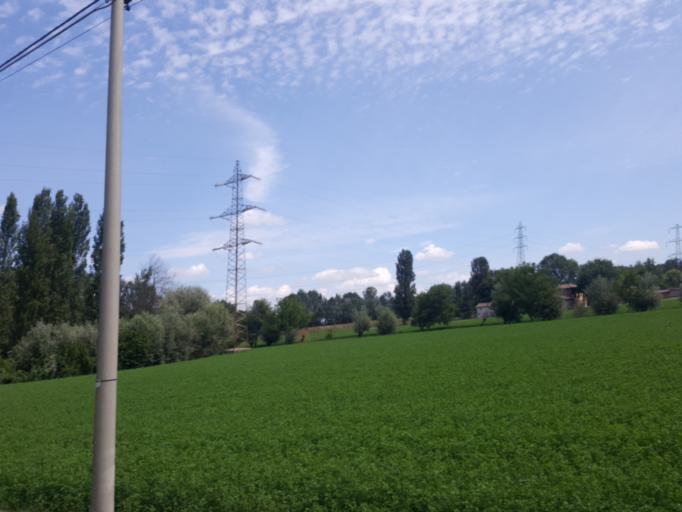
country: IT
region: Emilia-Romagna
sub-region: Provincia di Bologna
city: Anzola dell'Emilia
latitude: 44.5254
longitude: 11.2261
